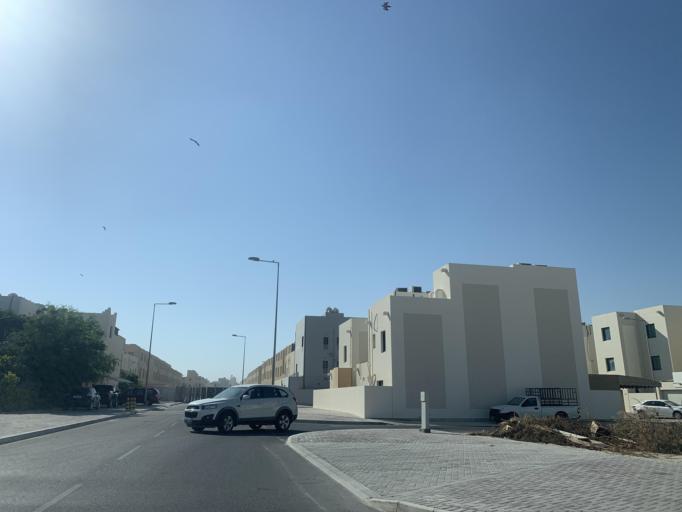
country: BH
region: Central Governorate
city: Madinat Hamad
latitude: 26.1227
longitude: 50.4837
